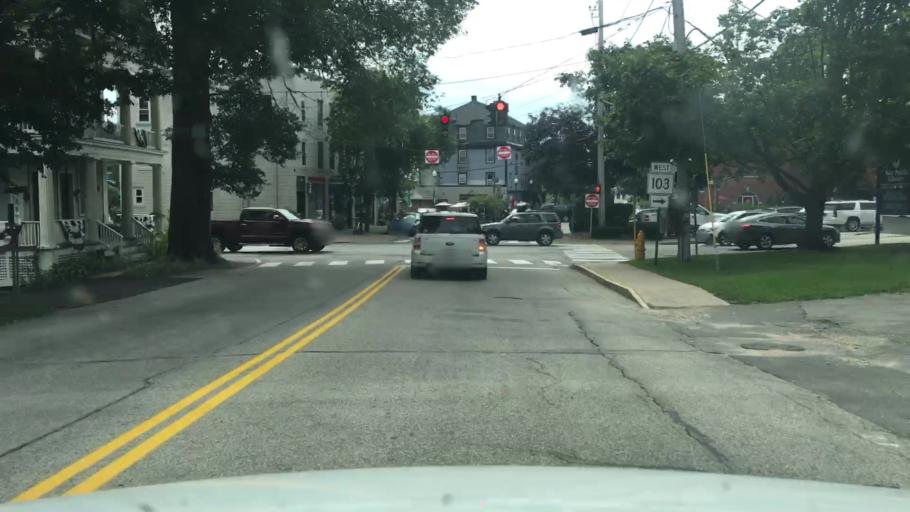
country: US
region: Maine
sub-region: York County
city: Kittery
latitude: 43.0866
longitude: -70.7430
